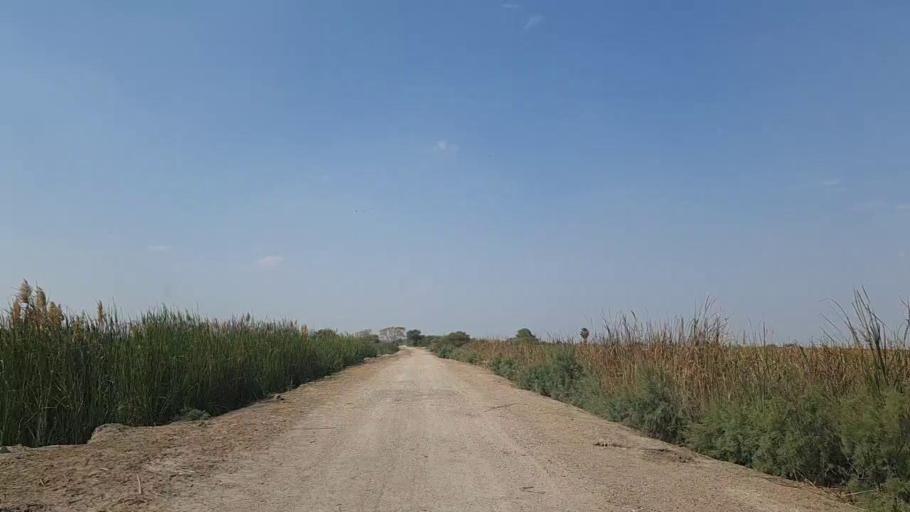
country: PK
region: Sindh
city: Jati
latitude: 24.5101
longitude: 68.2955
